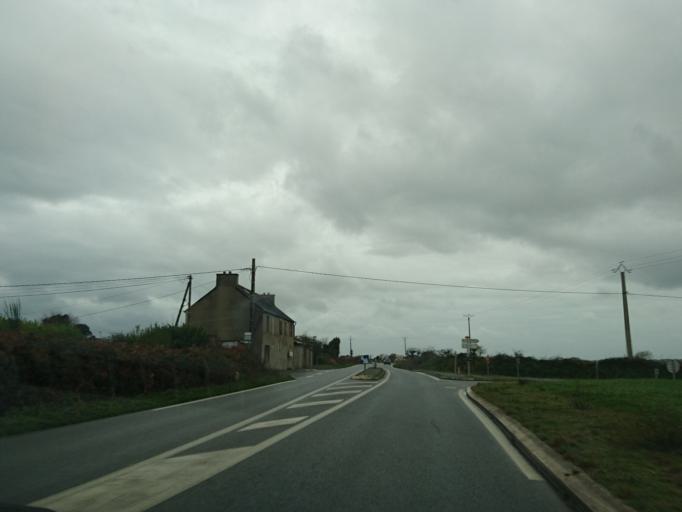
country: FR
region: Brittany
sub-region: Departement du Finistere
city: Plouzane
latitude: 48.3618
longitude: -4.6152
